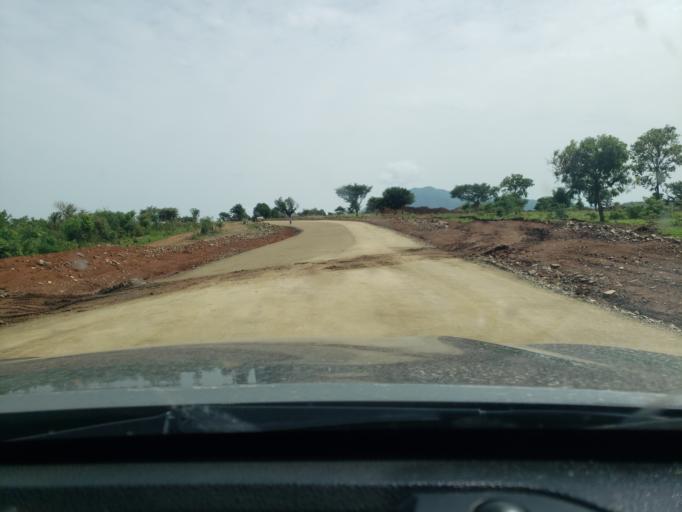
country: ET
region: Oromiya
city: Mendi
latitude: 10.1196
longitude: 35.1516
